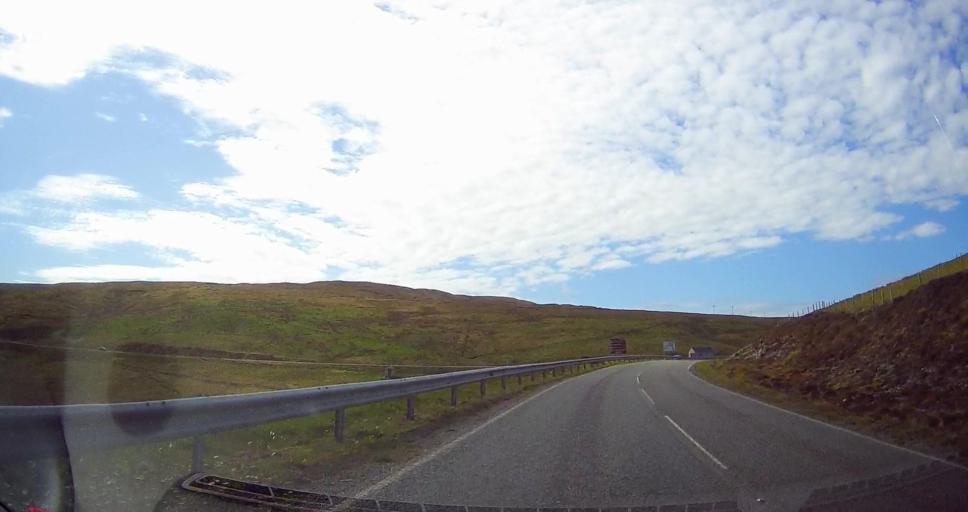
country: GB
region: Scotland
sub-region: Shetland Islands
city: Sandwick
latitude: 59.9888
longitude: -1.2841
